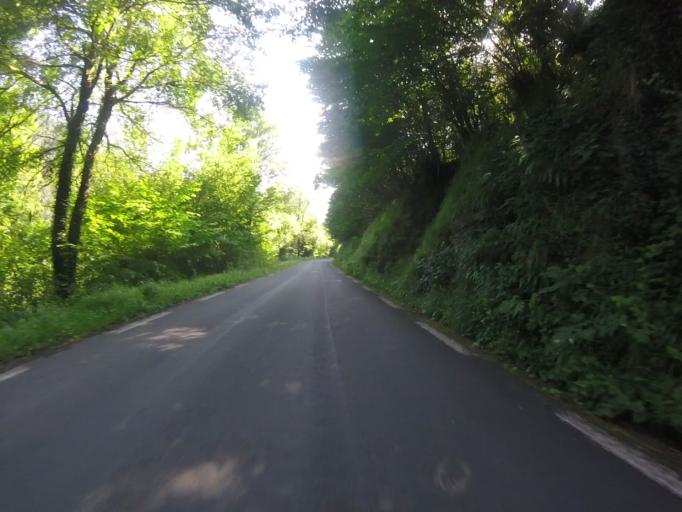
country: ES
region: Basque Country
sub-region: Provincia de Guipuzcoa
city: Ormaiztegui
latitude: 43.0723
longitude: -2.2321
